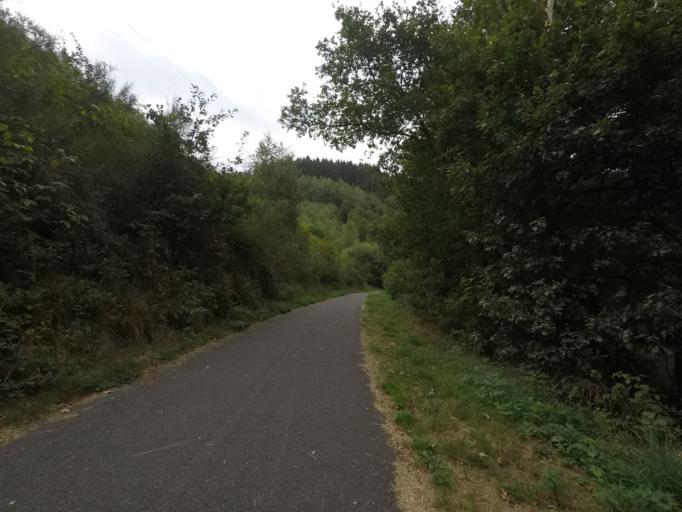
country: BE
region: Wallonia
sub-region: Province du Luxembourg
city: Martelange
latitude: 49.8433
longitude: 5.7266
